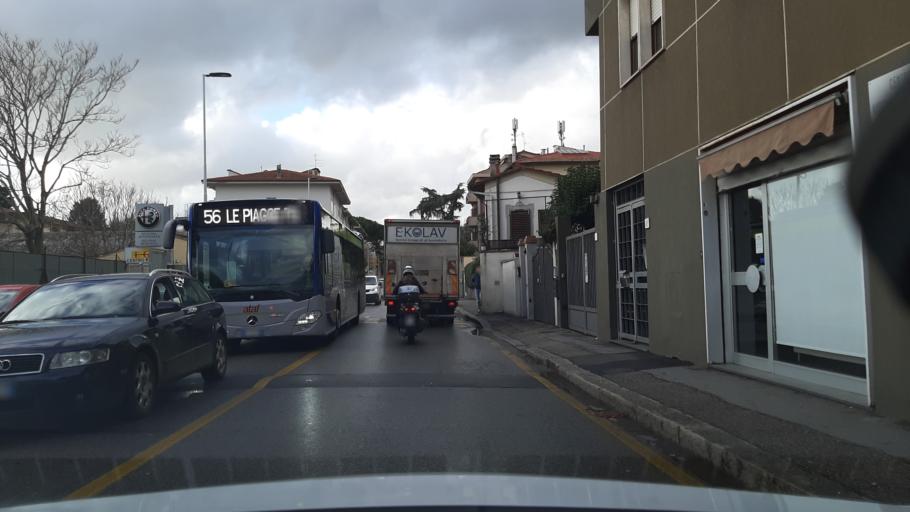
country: IT
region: Tuscany
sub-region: Province of Florence
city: Florence
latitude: 43.8041
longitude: 11.2444
